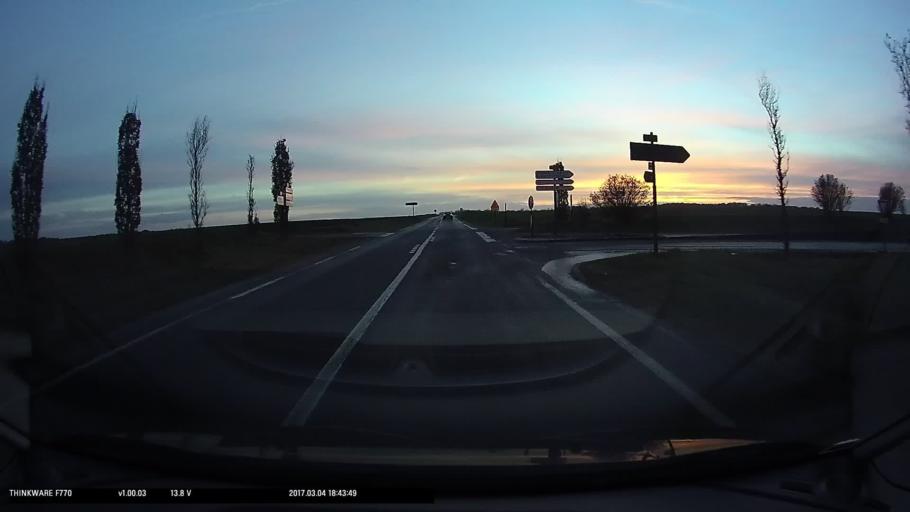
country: FR
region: Ile-de-France
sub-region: Departement du Val-d'Oise
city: Marines
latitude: 49.1419
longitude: 1.9676
